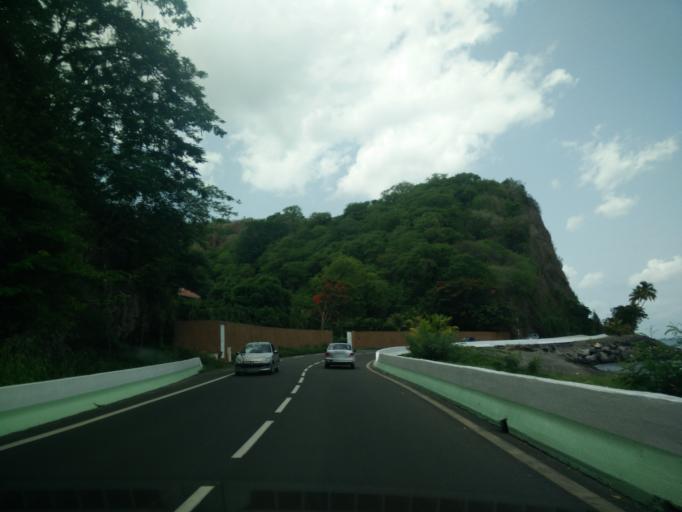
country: MQ
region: Martinique
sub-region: Martinique
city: Saint-Pierre
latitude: 14.7203
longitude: -61.1820
